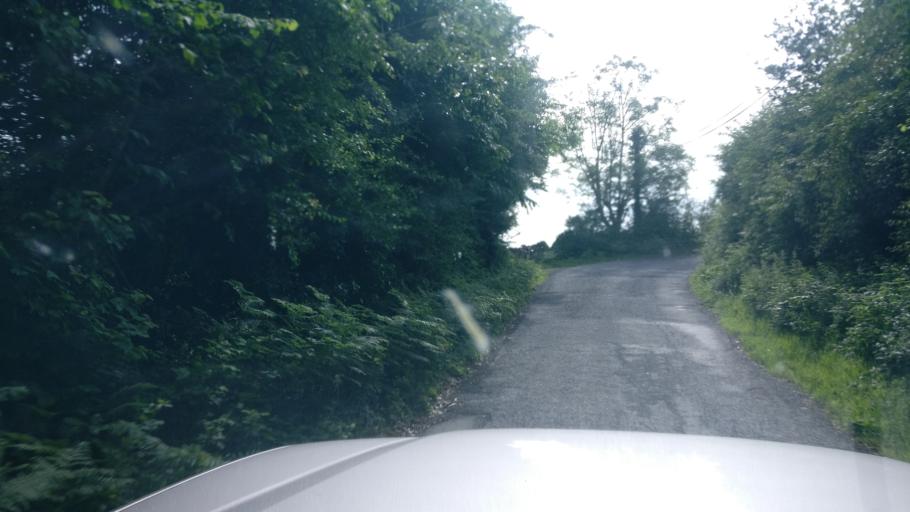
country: IE
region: Connaught
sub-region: County Galway
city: Gort
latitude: 53.1024
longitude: -8.7098
